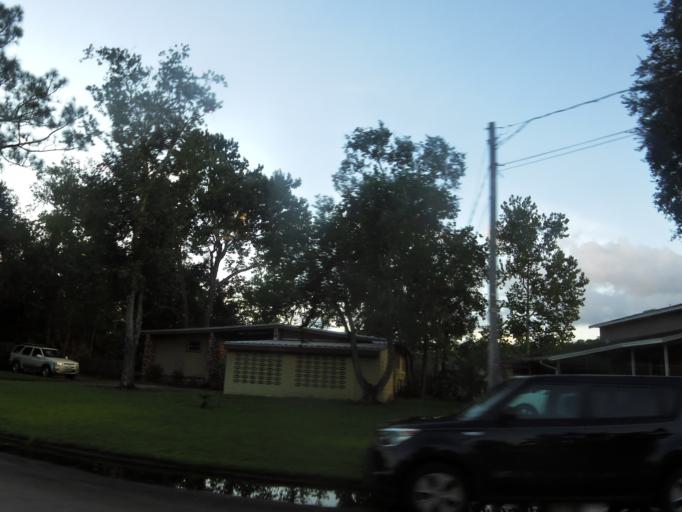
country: US
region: Florida
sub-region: Duval County
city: Jacksonville
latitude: 30.2390
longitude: -81.6090
